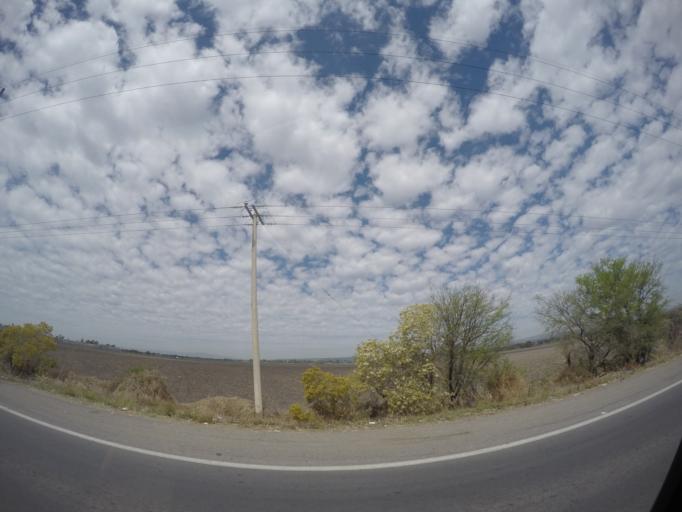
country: MX
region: Guanajuato
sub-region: Leon
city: San Antonio de los Tepetates
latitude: 21.0417
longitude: -101.6921
